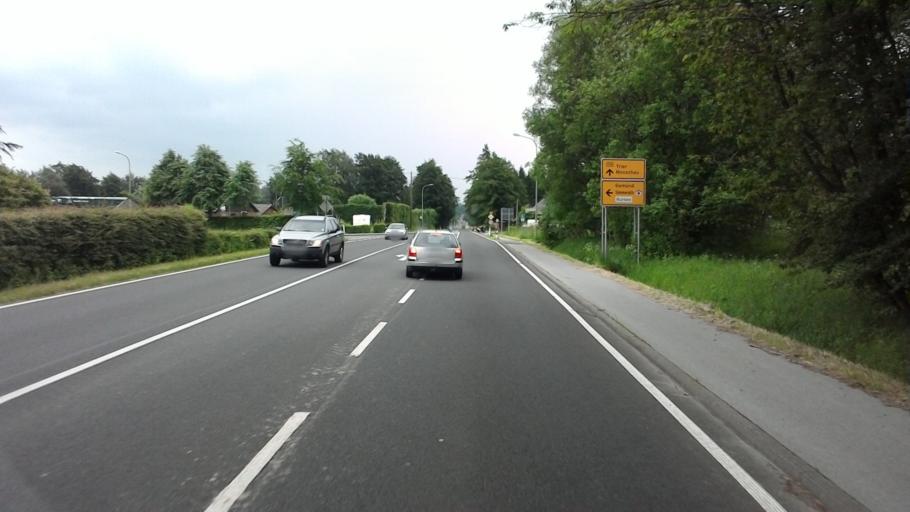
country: DE
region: North Rhine-Westphalia
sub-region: Regierungsbezirk Koln
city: Monschau
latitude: 50.5995
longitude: 6.2491
